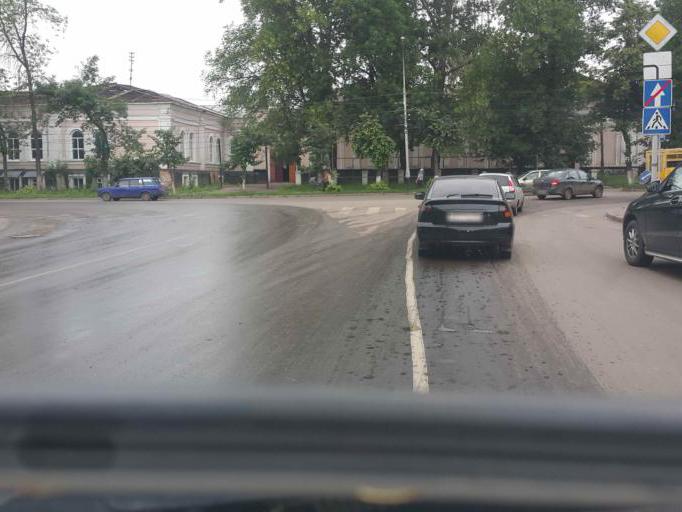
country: RU
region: Tambov
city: Michurinsk
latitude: 52.8945
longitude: 40.4983
